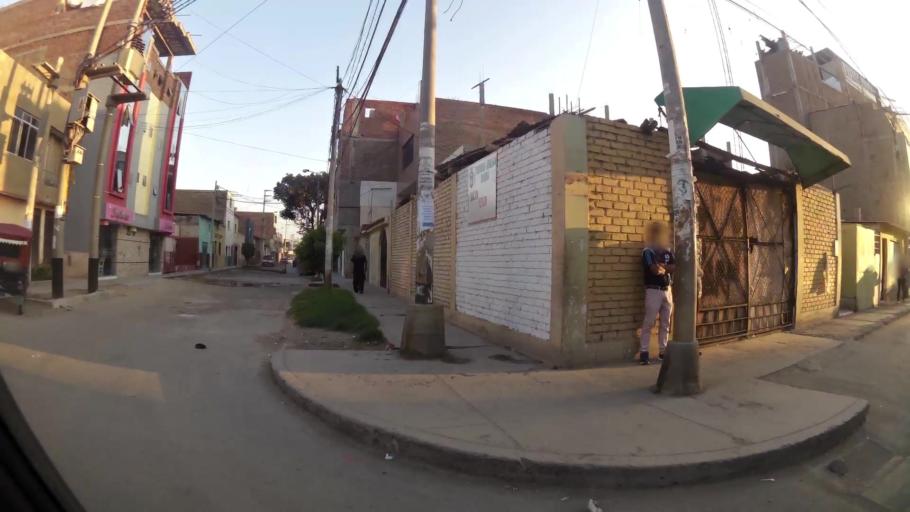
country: PE
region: Lambayeque
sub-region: Provincia de Chiclayo
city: Santa Rosa
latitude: -6.7681
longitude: -79.8352
